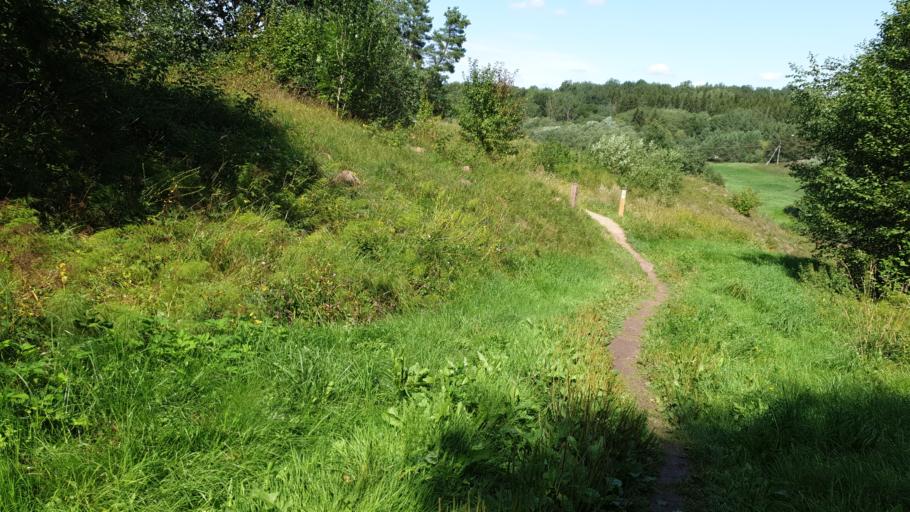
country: LT
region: Vilnius County
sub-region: Vilniaus Rajonas
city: Vievis
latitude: 54.8236
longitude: 24.9445
